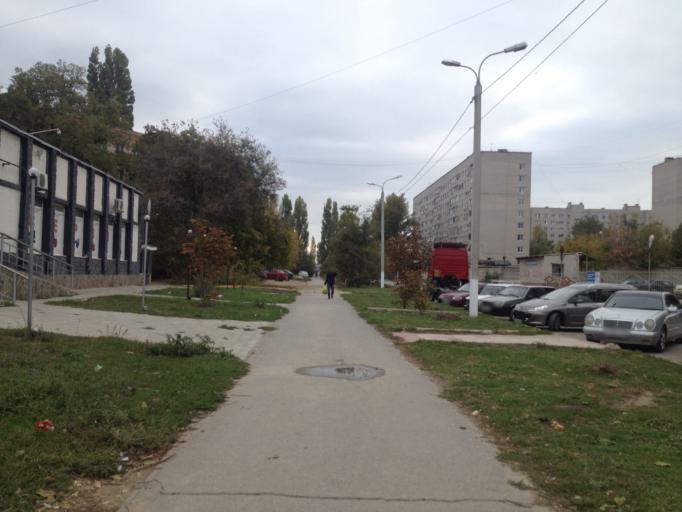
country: RU
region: Volgograd
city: Volgograd
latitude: 48.7371
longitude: 44.4881
